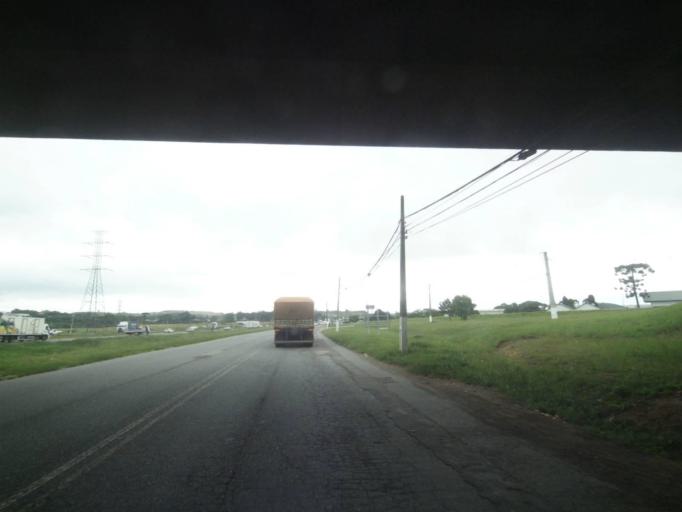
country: BR
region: Parana
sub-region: Araucaria
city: Araucaria
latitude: -25.5226
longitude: -49.3324
